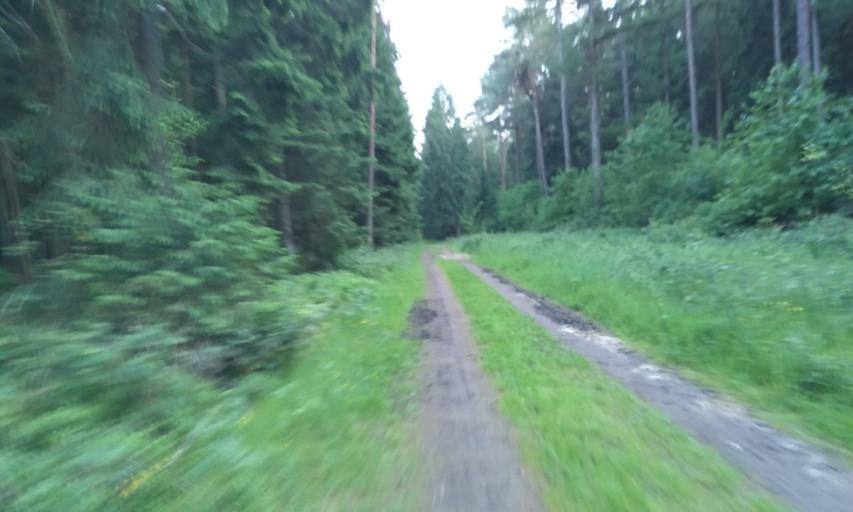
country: DE
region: Lower Saxony
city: Dollern
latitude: 53.5242
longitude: 9.5253
